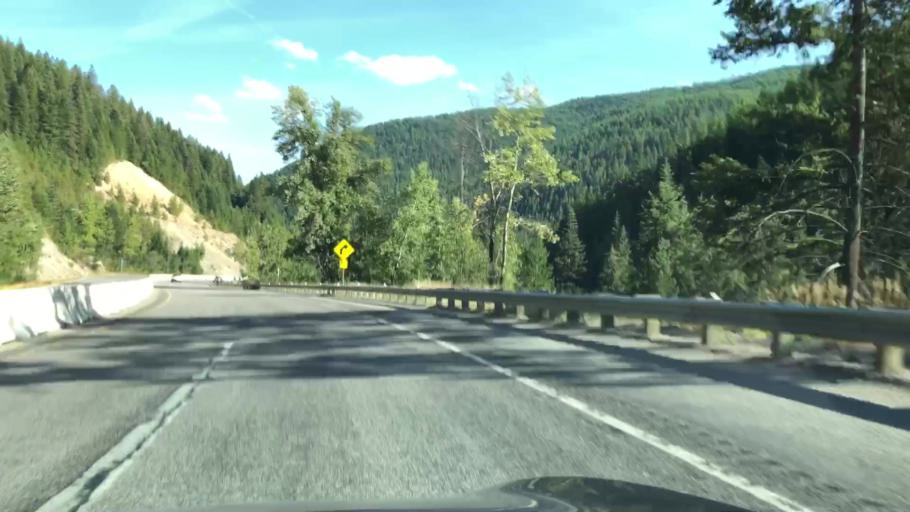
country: US
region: Montana
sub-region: Sanders County
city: Thompson Falls
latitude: 47.3989
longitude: -115.4602
